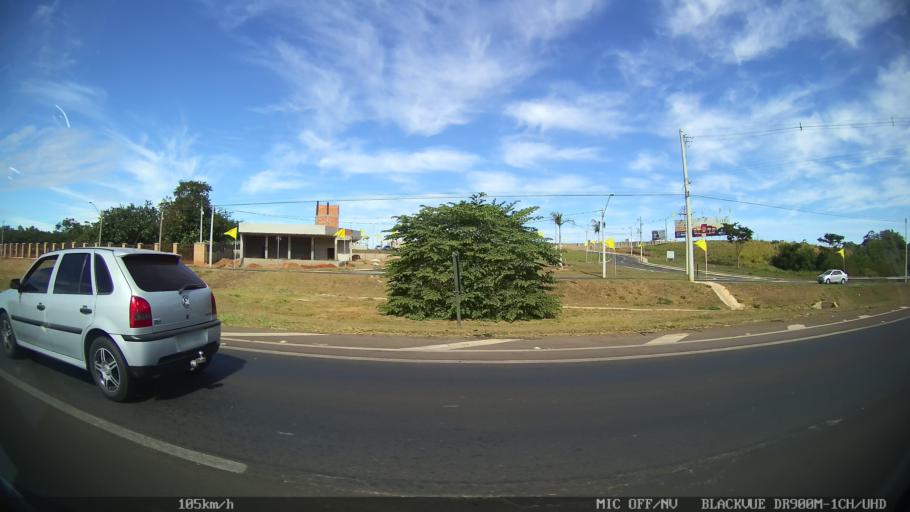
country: BR
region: Sao Paulo
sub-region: Sao Jose Do Rio Preto
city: Sao Jose do Rio Preto
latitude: -20.8148
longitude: -49.4699
